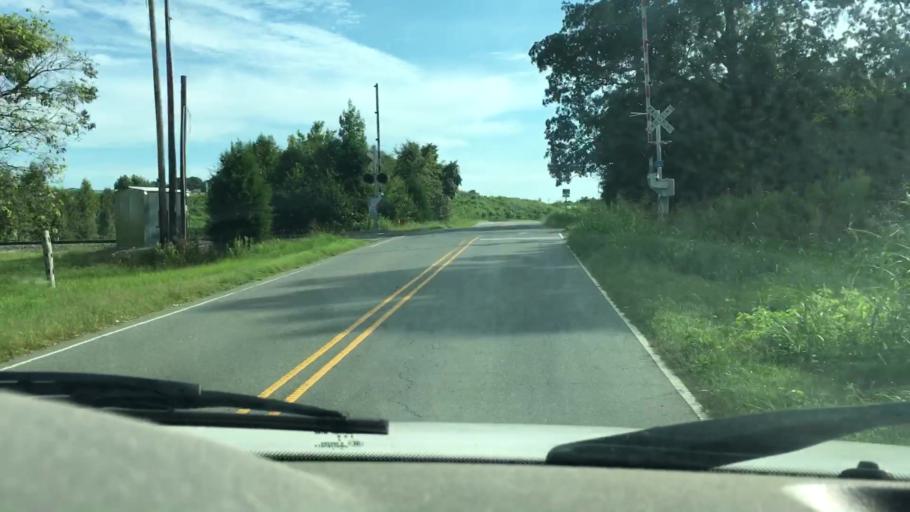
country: US
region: North Carolina
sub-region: Mecklenburg County
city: Huntersville
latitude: 35.3643
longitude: -80.8192
